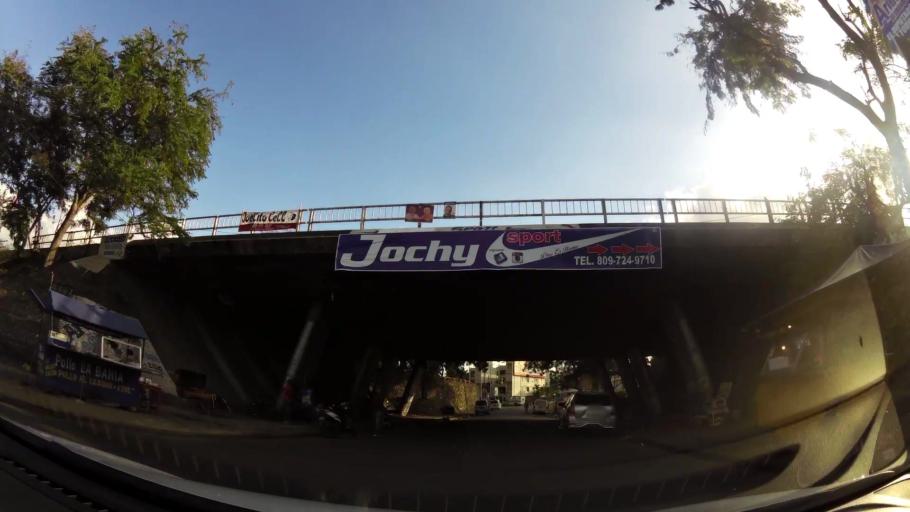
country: DO
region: Santiago
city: Santiago de los Caballeros
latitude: 19.4581
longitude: -70.7080
